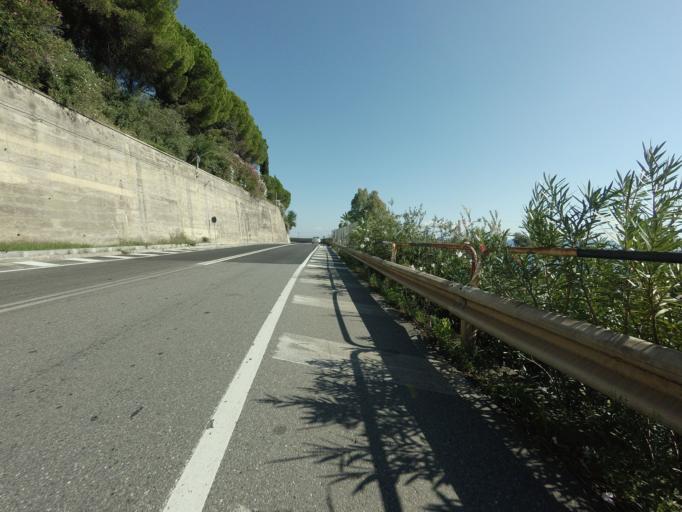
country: IT
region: Sicily
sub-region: Messina
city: Taormina
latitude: 37.8663
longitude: 15.2974
